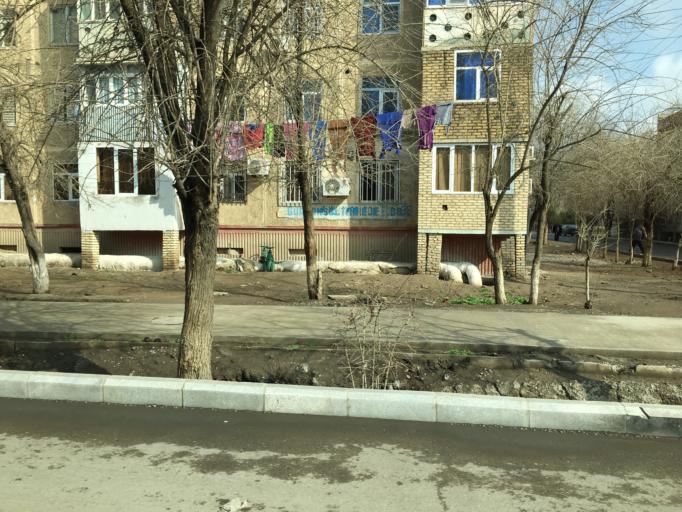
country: TM
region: Mary
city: Mary
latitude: 37.5933
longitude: 61.8305
